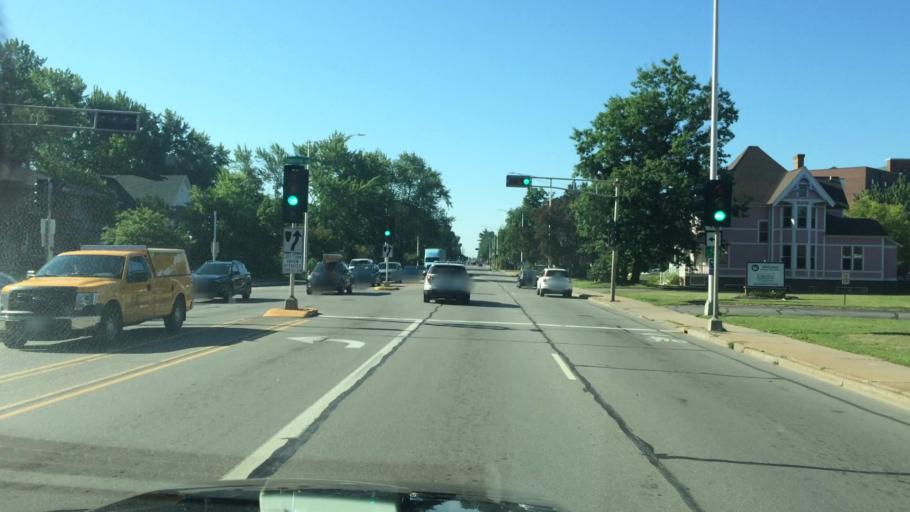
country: US
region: Wisconsin
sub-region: Marathon County
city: Wausau
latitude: 44.9453
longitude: -89.6206
